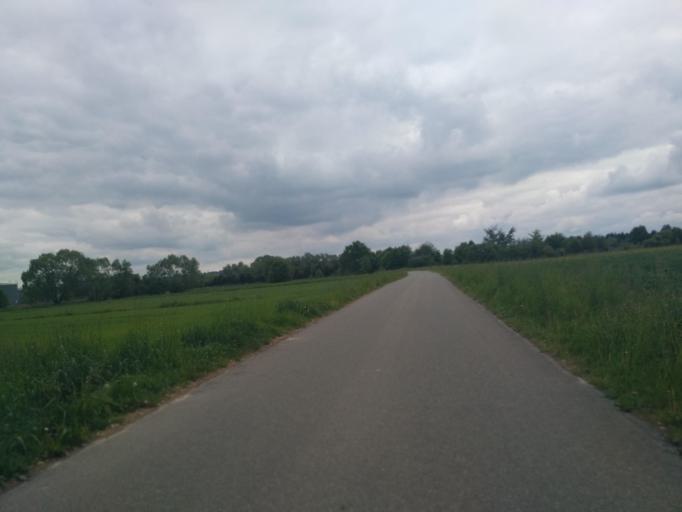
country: PL
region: Subcarpathian Voivodeship
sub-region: Powiat krosnienski
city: Jedlicze
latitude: 49.7059
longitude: 21.6766
